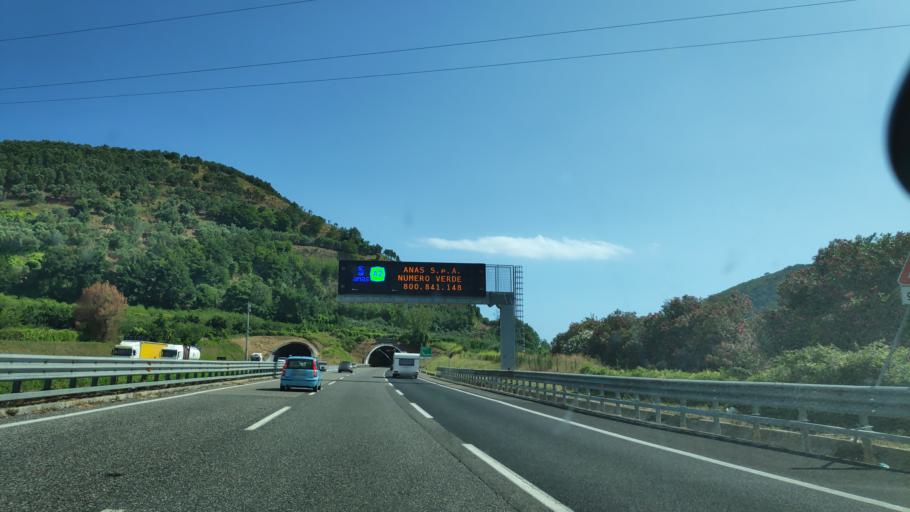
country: IT
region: Campania
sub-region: Provincia di Salerno
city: Pezzano-Filetta
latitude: 40.6796
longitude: 14.8571
